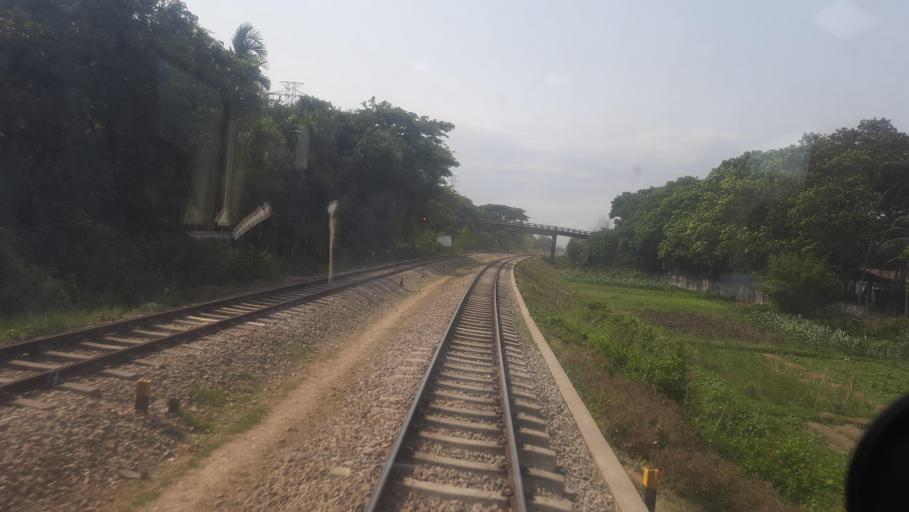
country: BD
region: Chittagong
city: Chittagong
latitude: 22.4249
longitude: 91.7508
